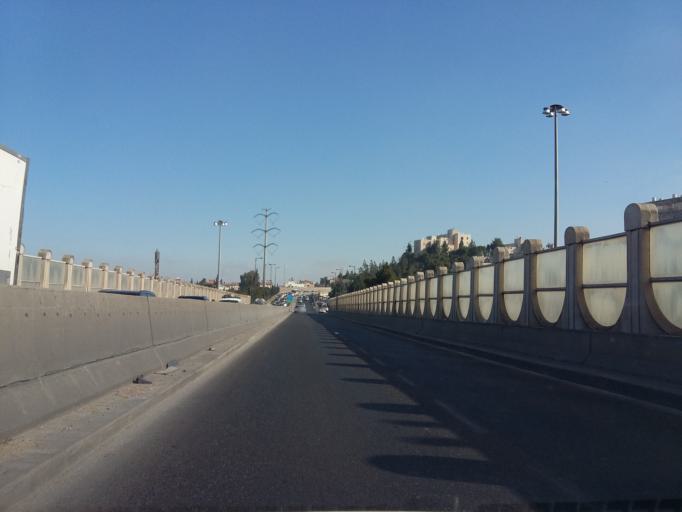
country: PS
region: West Bank
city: East Jerusalem
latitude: 31.8044
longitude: 35.2351
